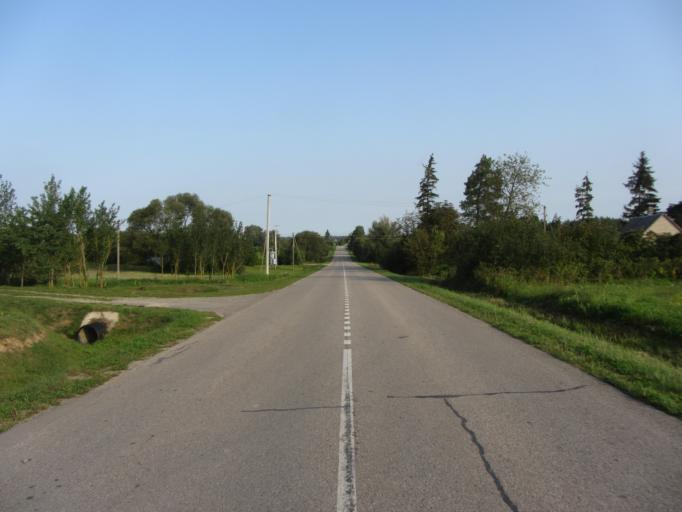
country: LT
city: Lazdijai
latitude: 54.3243
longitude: 23.4350
